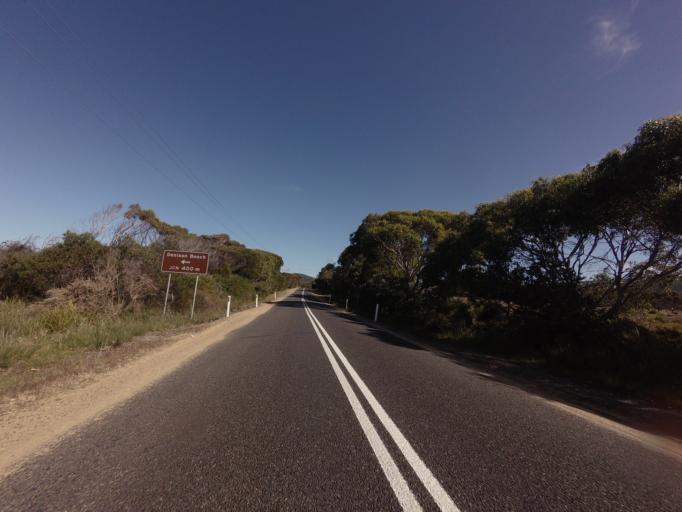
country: AU
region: Tasmania
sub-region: Break O'Day
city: St Helens
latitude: -41.8231
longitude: 148.2632
